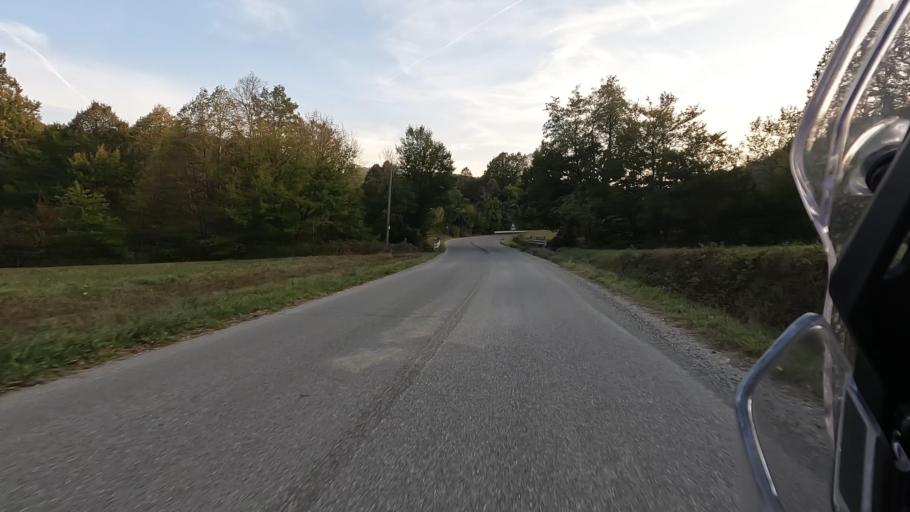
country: IT
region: Liguria
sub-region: Provincia di Savona
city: Mioglia
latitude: 44.5079
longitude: 8.4359
